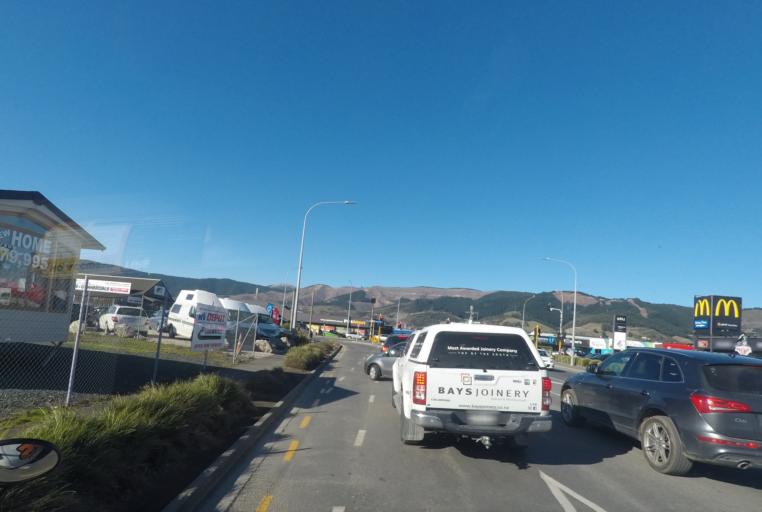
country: NZ
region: Tasman
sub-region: Tasman District
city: Richmond
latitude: -41.3360
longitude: 173.1813
